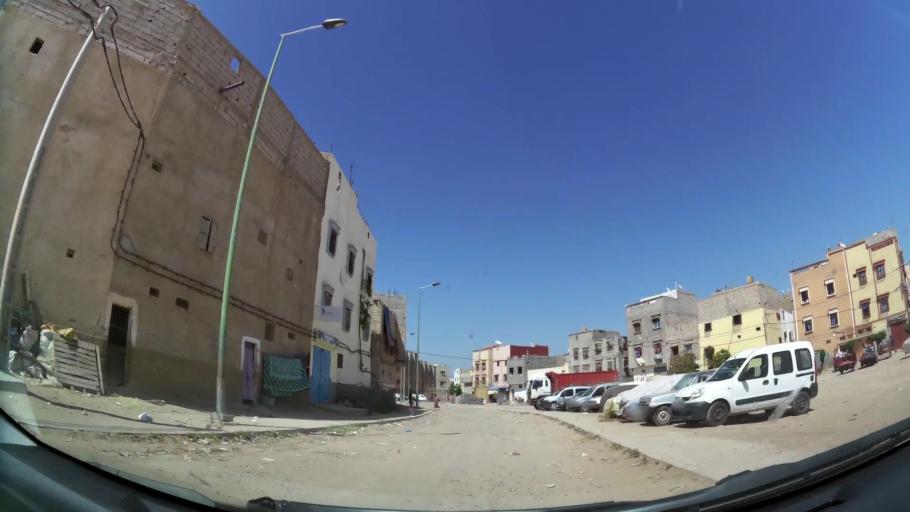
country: MA
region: Souss-Massa-Draa
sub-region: Inezgane-Ait Mellou
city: Inezgane
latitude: 30.3449
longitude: -9.5390
